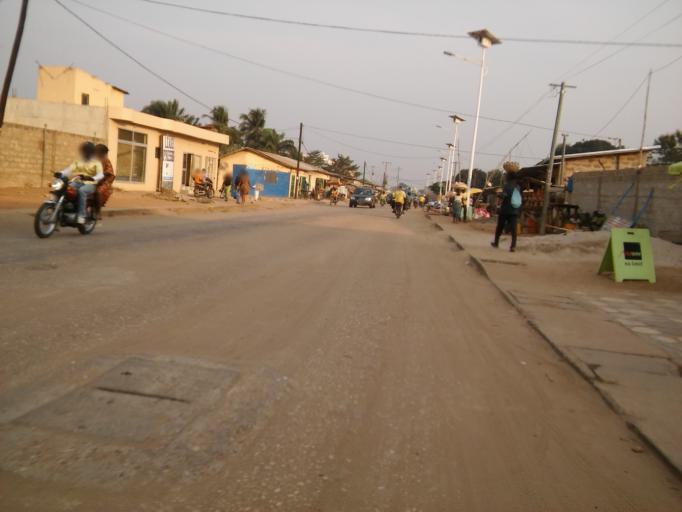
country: BJ
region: Atlantique
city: Abomey-Calavi
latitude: 6.4026
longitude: 2.3394
